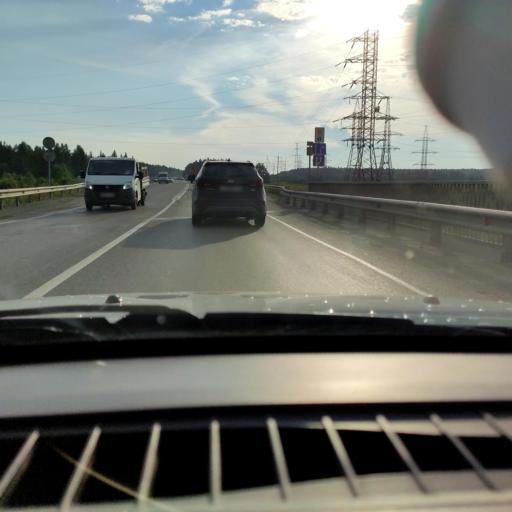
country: RU
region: Sverdlovsk
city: Revda
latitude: 56.8278
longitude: 59.9393
